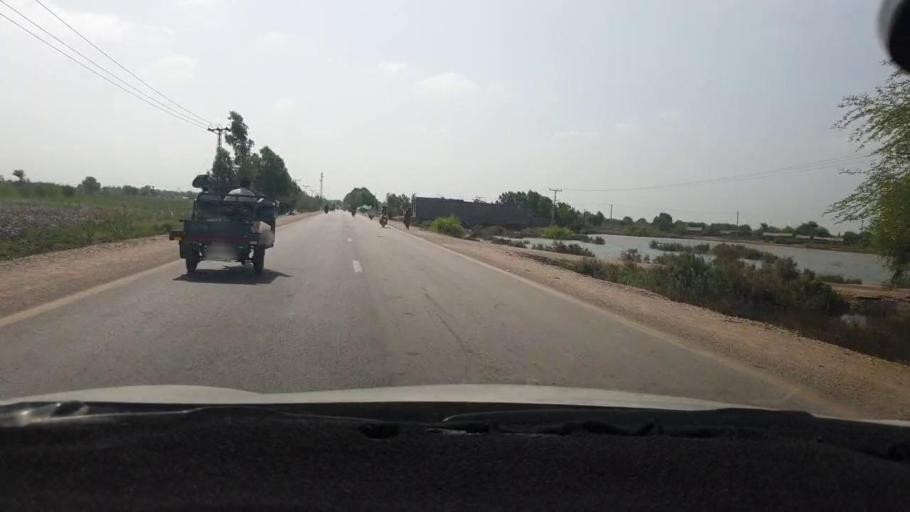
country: PK
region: Sindh
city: Mirpur Khas
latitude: 25.7162
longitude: 69.1219
